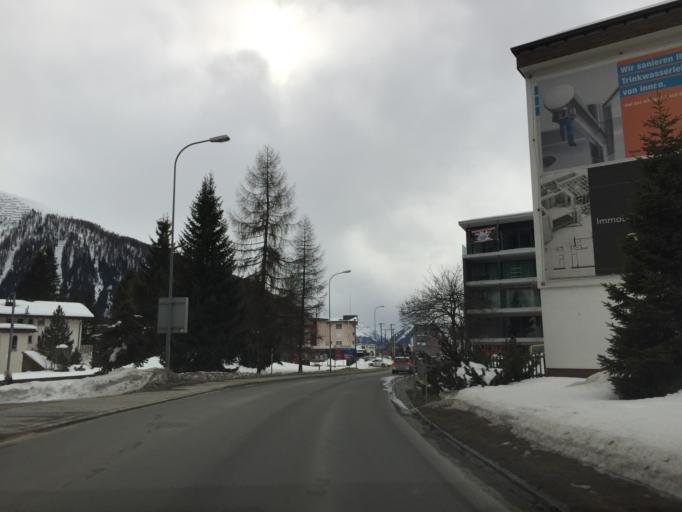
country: CH
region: Grisons
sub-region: Praettigau/Davos District
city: Davos
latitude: 46.8127
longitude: 9.8452
